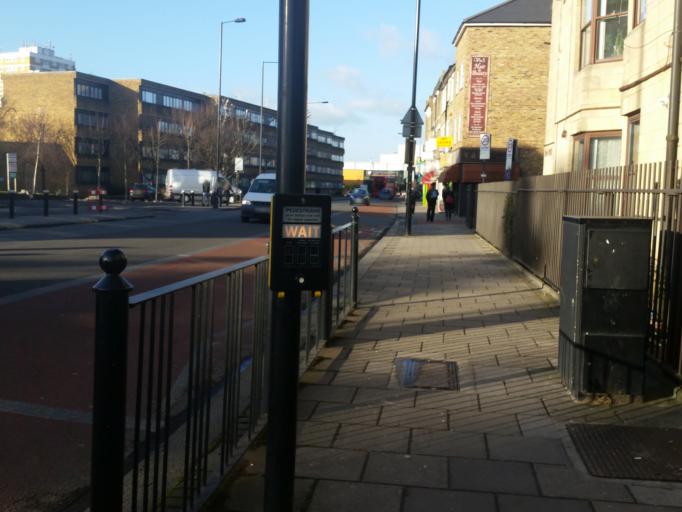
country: GB
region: England
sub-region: Greater London
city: Wood Green
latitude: 51.6009
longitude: -0.1116
